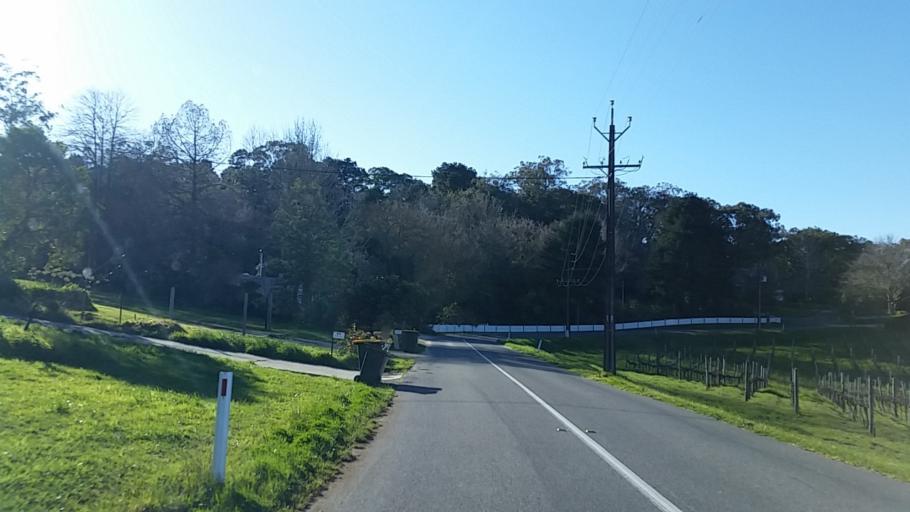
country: AU
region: South Australia
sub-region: Adelaide Hills
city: Adelaide Hills
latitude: -34.9502
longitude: 138.7220
